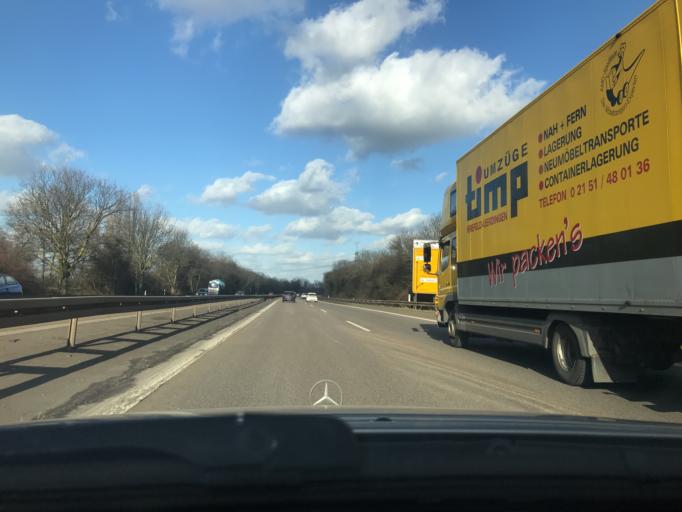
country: DE
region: North Rhine-Westphalia
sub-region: Regierungsbezirk Dusseldorf
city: Krefeld
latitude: 51.3772
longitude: 6.6425
